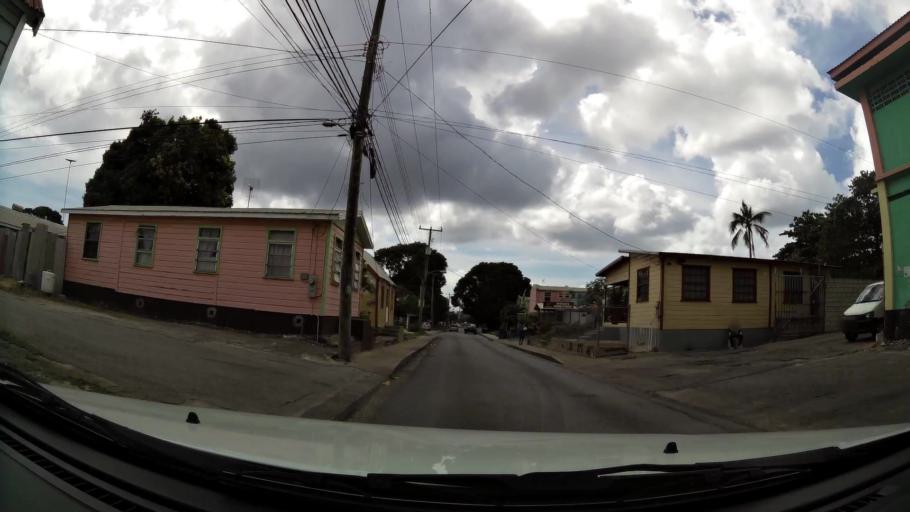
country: BB
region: Saint Michael
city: Bridgetown
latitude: 13.1184
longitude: -59.6200
